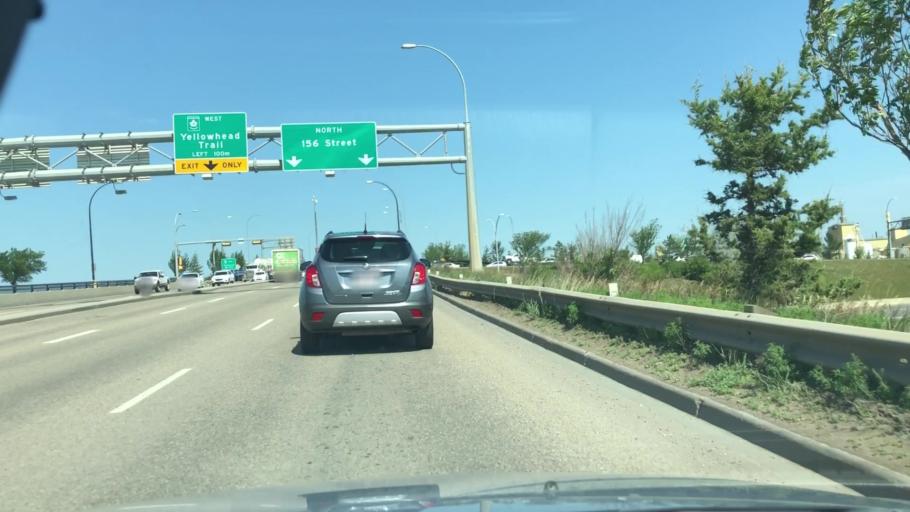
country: CA
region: Alberta
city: St. Albert
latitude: 53.5783
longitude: -113.5905
